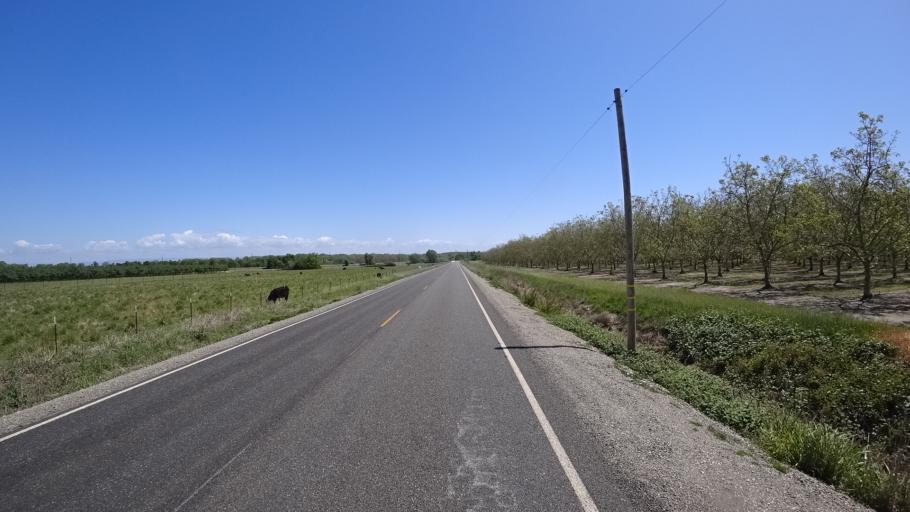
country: US
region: California
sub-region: Glenn County
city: Hamilton City
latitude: 39.7665
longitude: -122.0359
